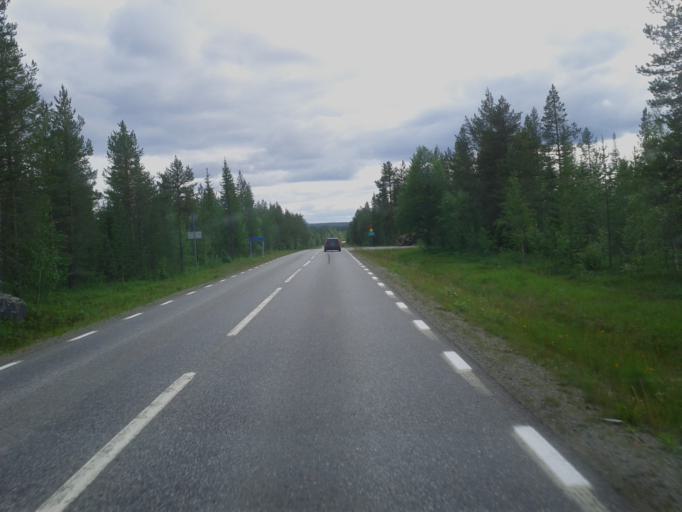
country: SE
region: Vaesterbotten
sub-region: Sorsele Kommun
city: Sorsele
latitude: 65.2271
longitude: 17.6505
